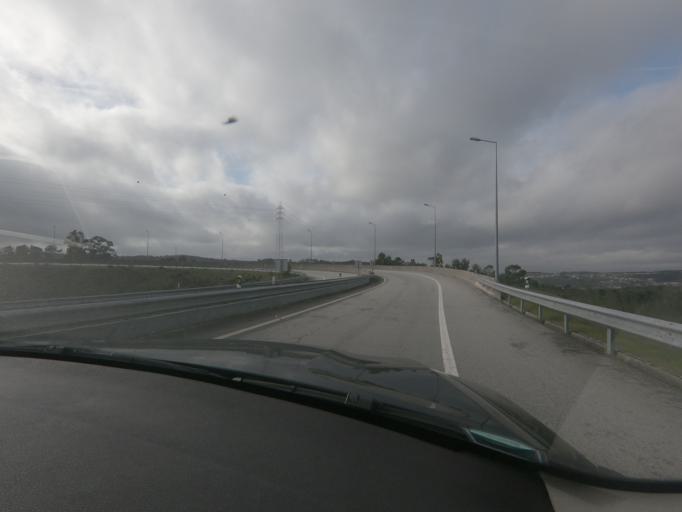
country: PT
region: Viseu
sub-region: Viseu
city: Campo
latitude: 40.7088
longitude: -7.9451
